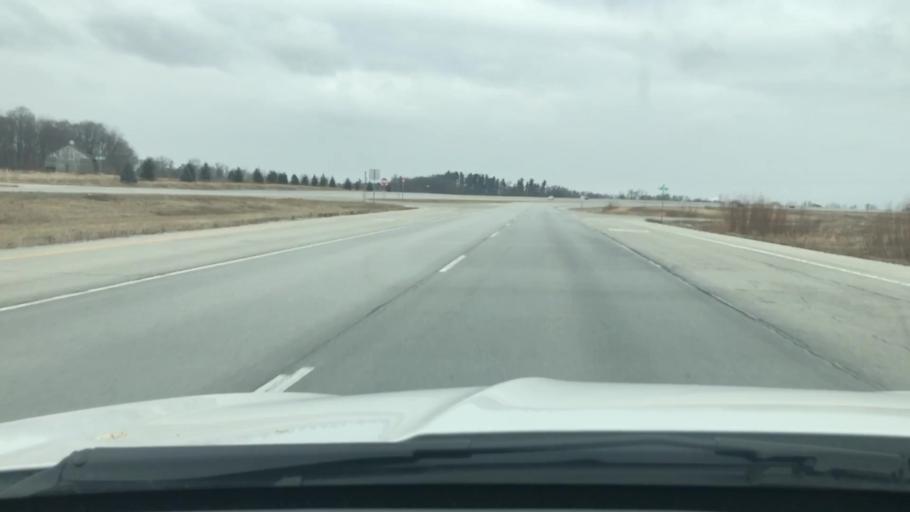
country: US
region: Indiana
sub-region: Cass County
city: Georgetown
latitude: 40.7058
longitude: -86.4560
